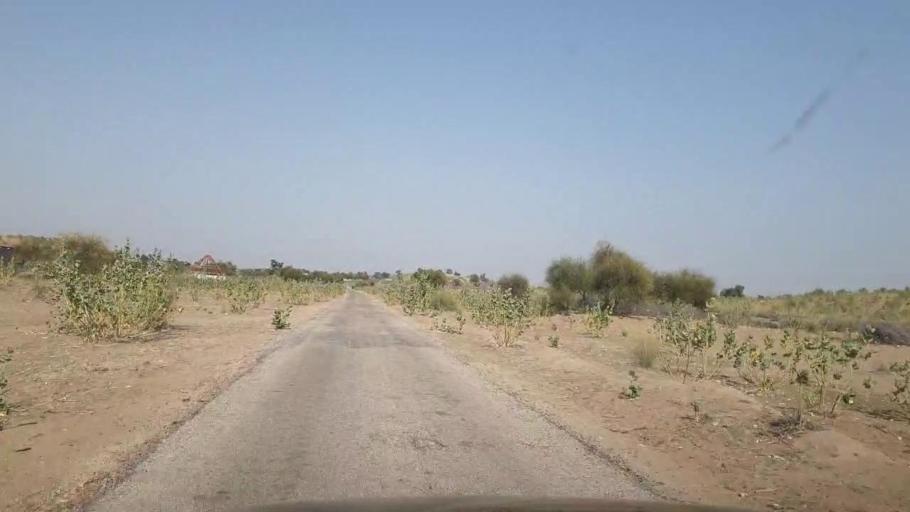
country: PK
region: Sindh
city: Islamkot
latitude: 25.1277
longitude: 70.4514
